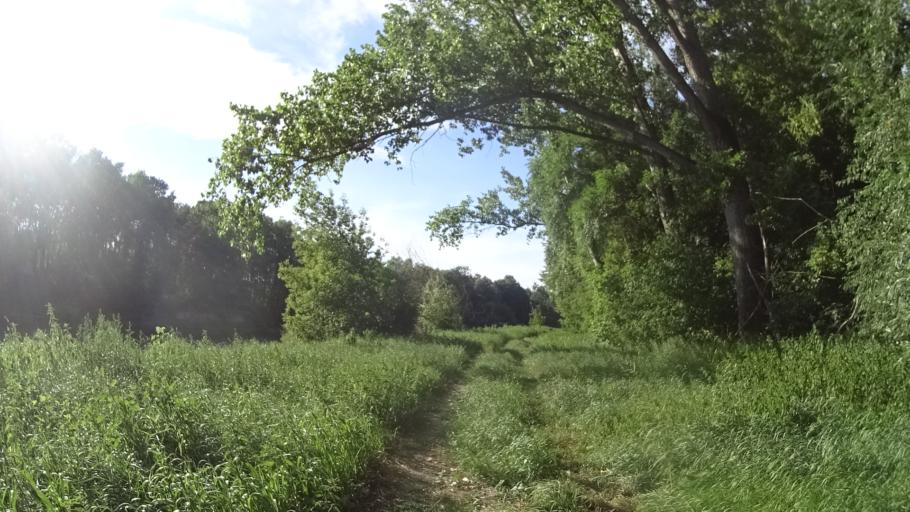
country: AT
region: Lower Austria
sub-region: Politischer Bezirk Mistelbach
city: Rabensburg
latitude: 48.6129
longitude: 16.9405
